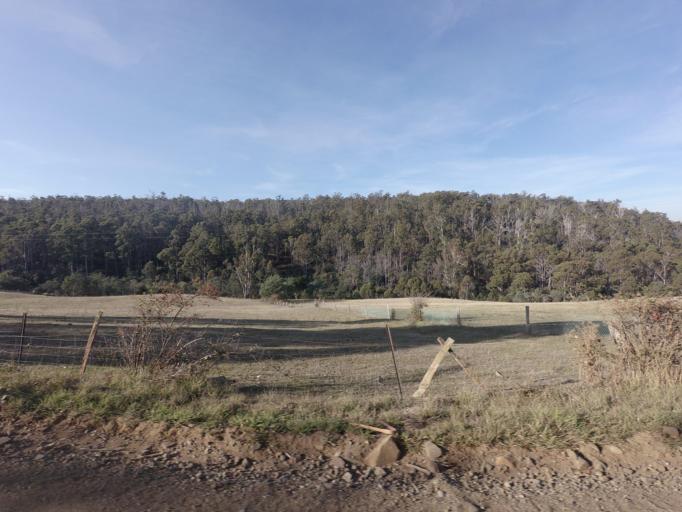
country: AU
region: Tasmania
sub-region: Brighton
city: Bridgewater
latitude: -42.4700
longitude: 147.3804
